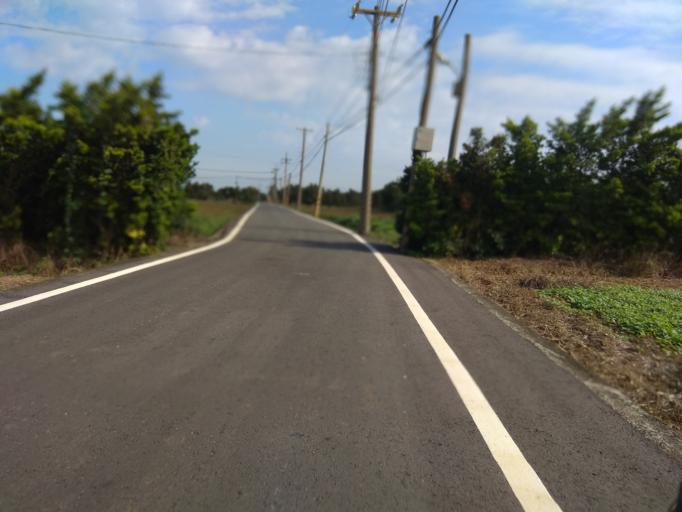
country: TW
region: Taiwan
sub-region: Hsinchu
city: Zhubei
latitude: 25.0024
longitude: 121.0469
